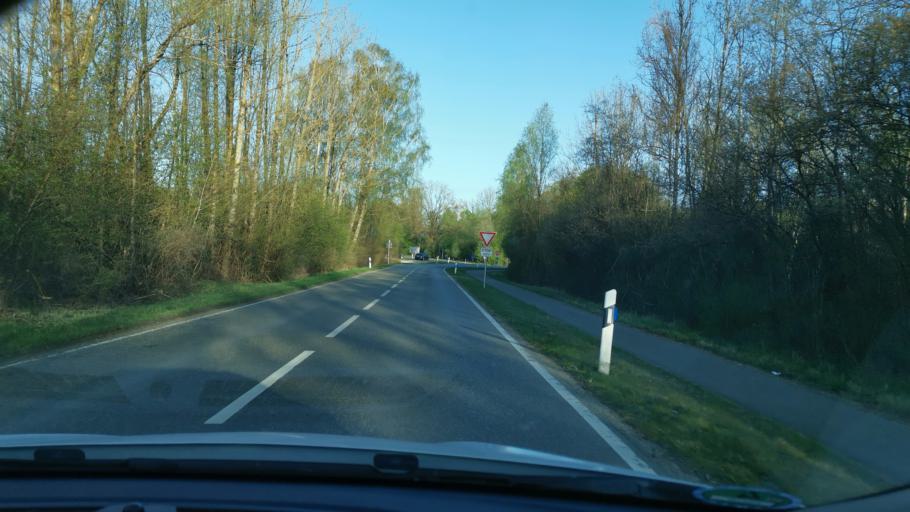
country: DE
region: Bavaria
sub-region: Swabia
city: Langweid
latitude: 48.4897
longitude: 10.8783
